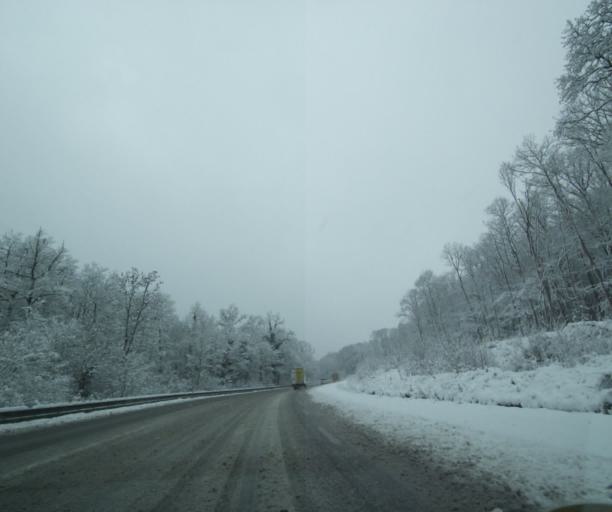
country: FR
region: Champagne-Ardenne
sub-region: Departement de la Haute-Marne
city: Saint-Dizier
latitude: 48.6126
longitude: 4.9176
